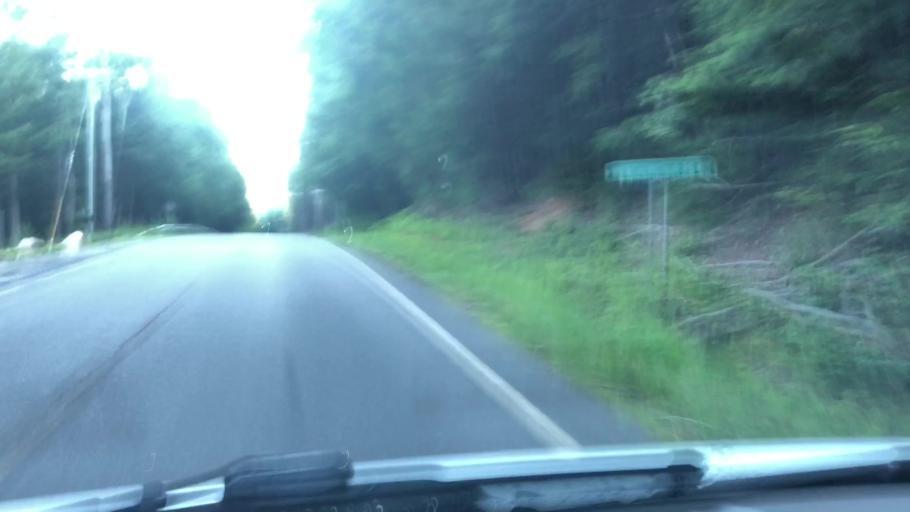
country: US
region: Massachusetts
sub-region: Berkshire County
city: Hinsdale
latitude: 42.4668
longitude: -72.9867
